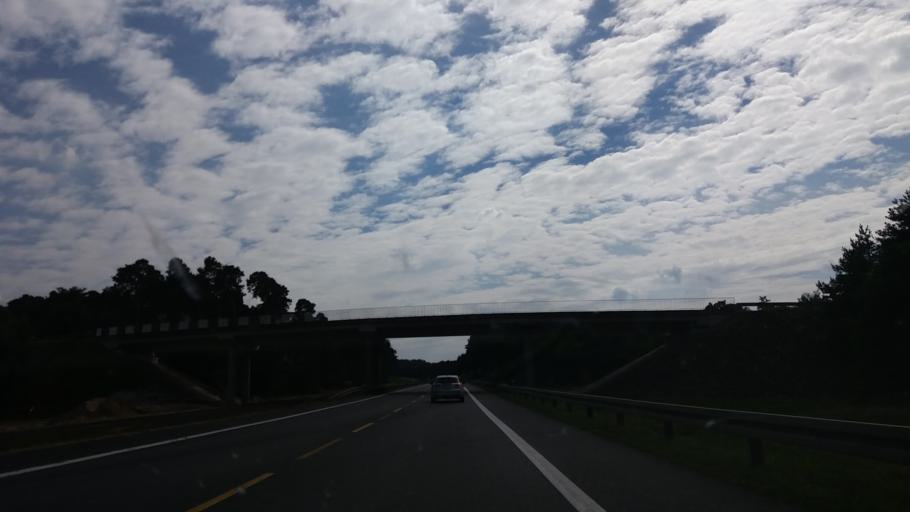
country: PL
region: Lubusz
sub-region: Zielona Gora
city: Zielona Gora
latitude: 51.9893
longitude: 15.5712
